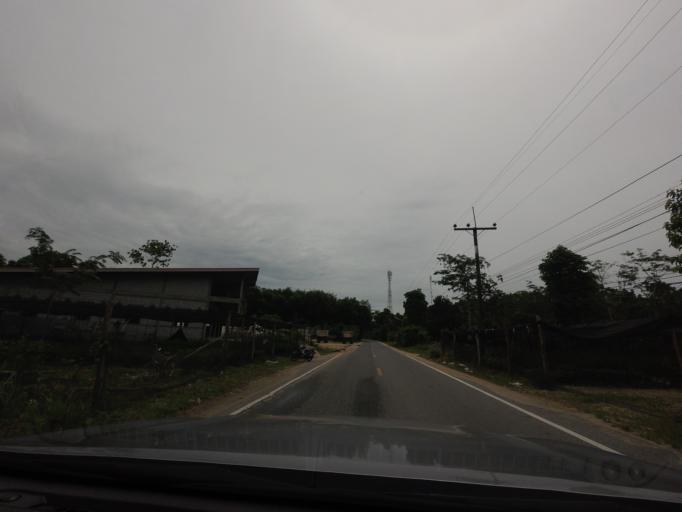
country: TH
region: Pattani
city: Kapho
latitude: 6.6318
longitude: 101.5482
